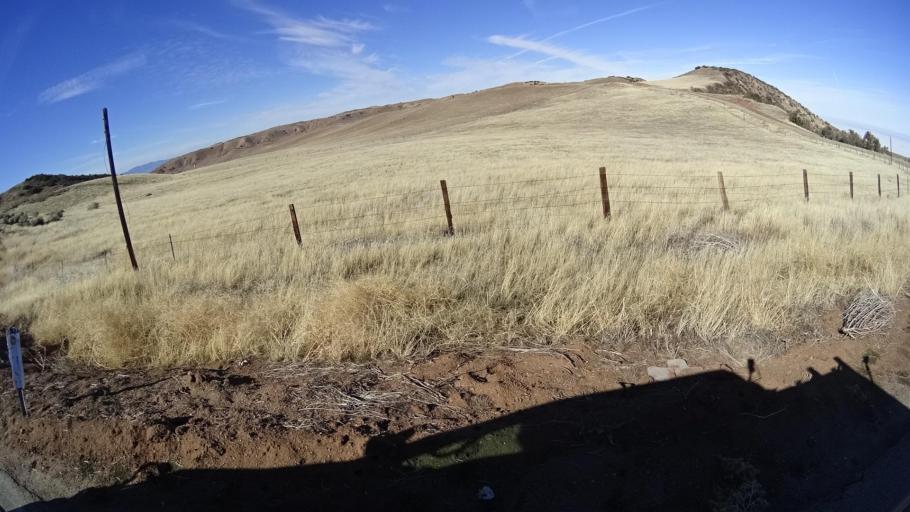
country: US
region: California
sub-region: Kern County
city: Maricopa
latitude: 34.8835
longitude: -119.3536
